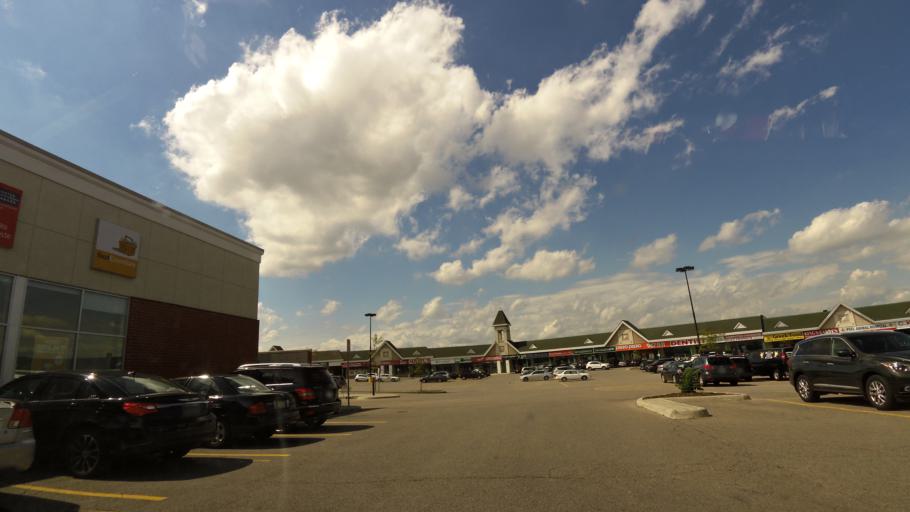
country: CA
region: Ontario
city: Brampton
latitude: 43.7597
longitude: -79.7283
